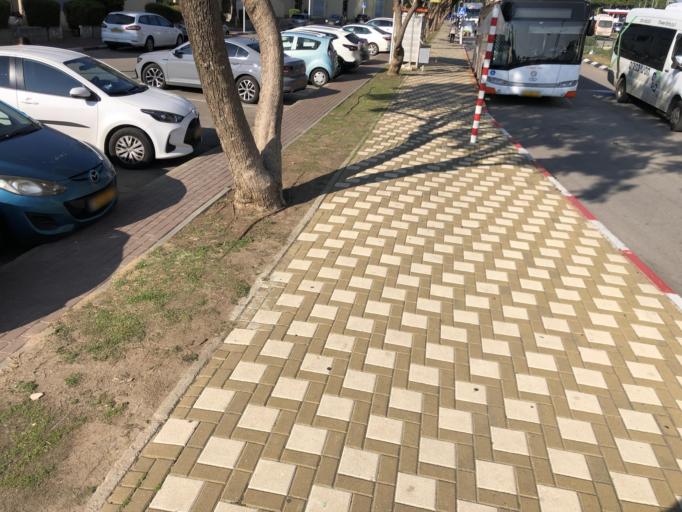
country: IL
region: Northern District
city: `Akko
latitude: 32.9189
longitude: 35.0919
